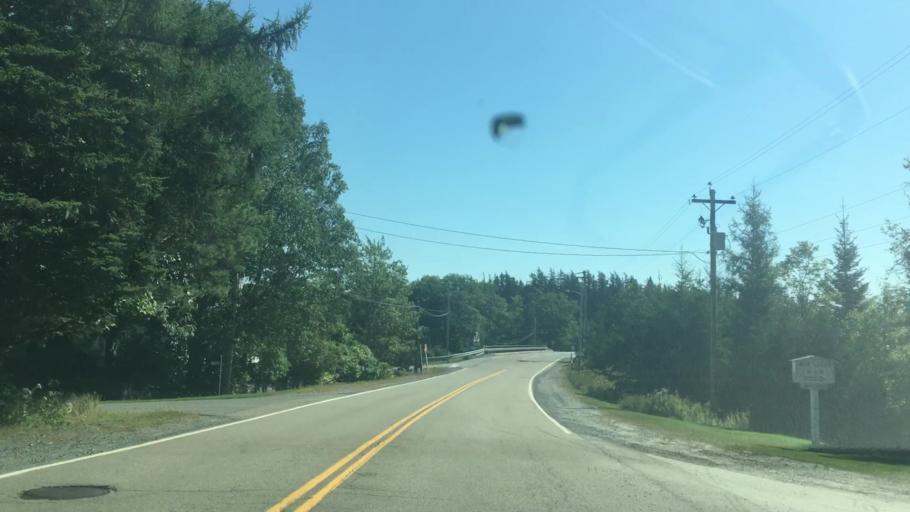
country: CA
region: Nova Scotia
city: Antigonish
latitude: 45.1440
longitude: -61.9854
